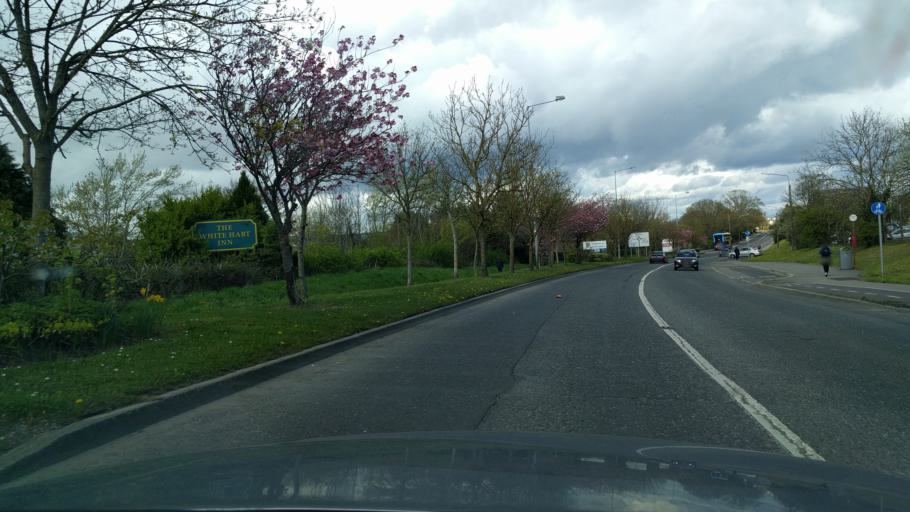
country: IE
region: Leinster
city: Balrothery
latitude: 53.5999
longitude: -6.1856
